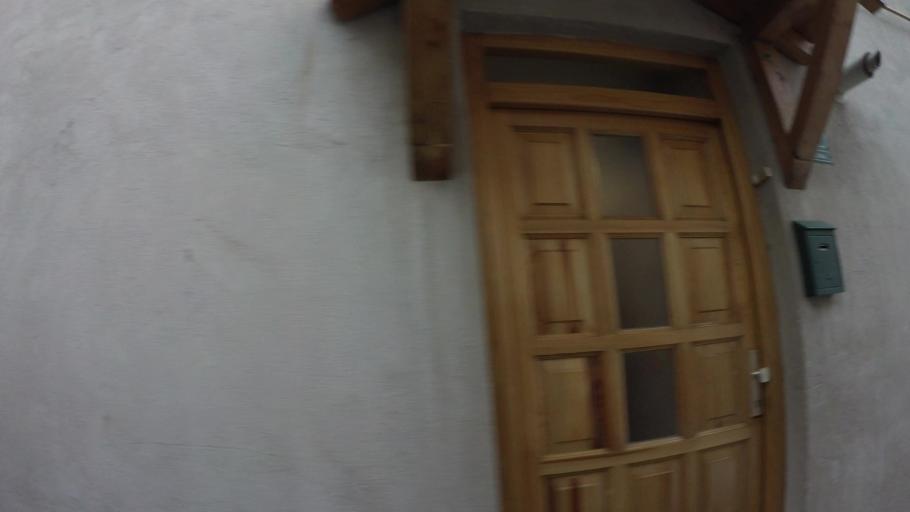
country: BA
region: Federation of Bosnia and Herzegovina
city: Kobilja Glava
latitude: 43.8635
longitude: 18.4348
